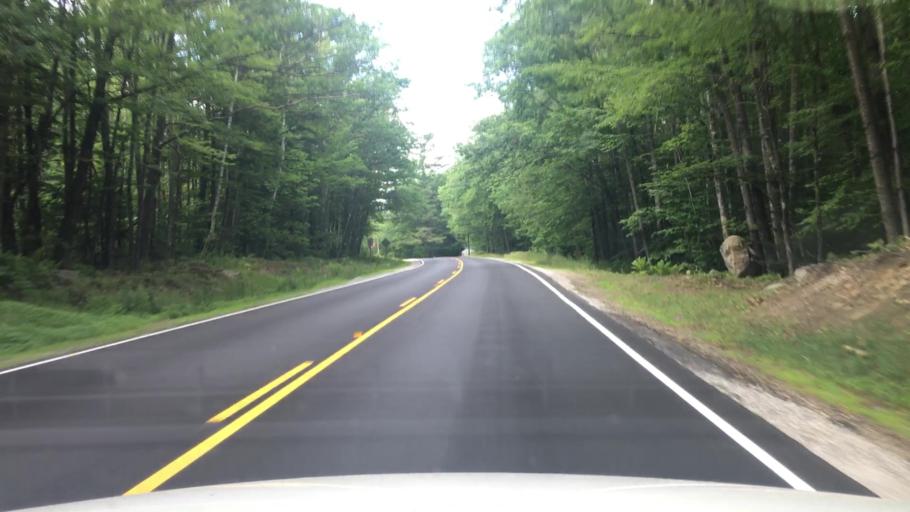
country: US
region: Maine
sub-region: Oxford County
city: West Paris
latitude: 44.3922
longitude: -70.6612
